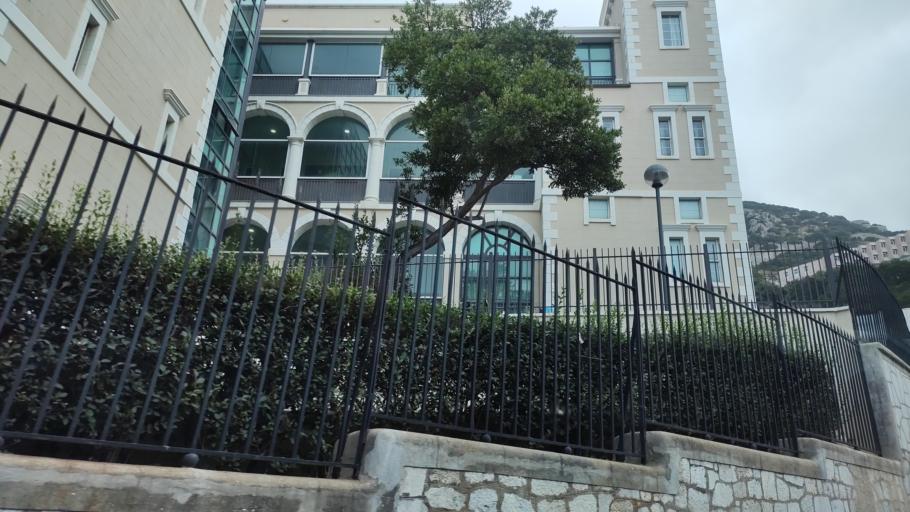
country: GI
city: Gibraltar
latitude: 36.1189
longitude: -5.3478
